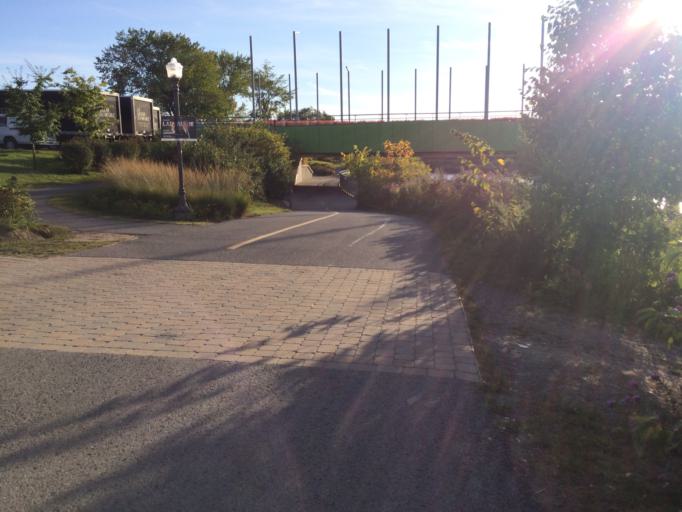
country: CA
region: Quebec
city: Quebec
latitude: 46.8132
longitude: -71.2502
